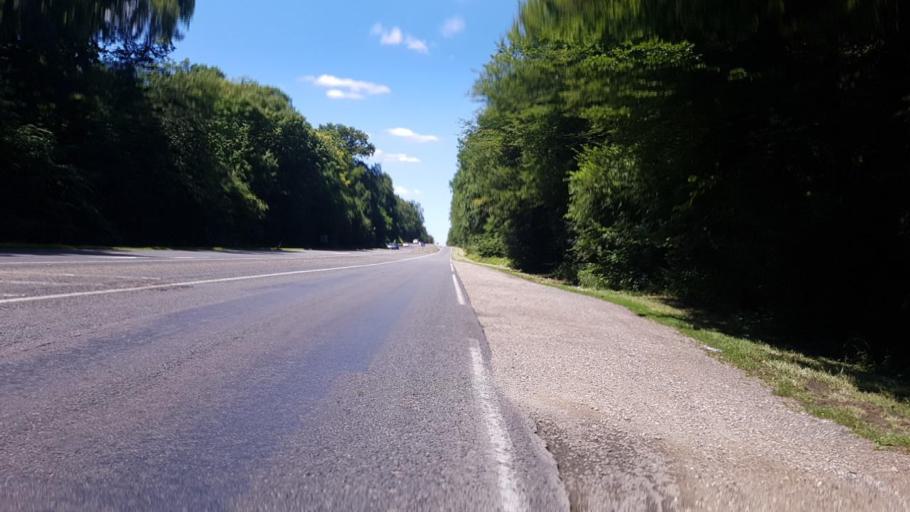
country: FR
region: Ile-de-France
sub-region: Departement de Seine-et-Marne
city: Saint-Jean-les-Deux-Jumeaux
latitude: 48.9590
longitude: 2.9897
